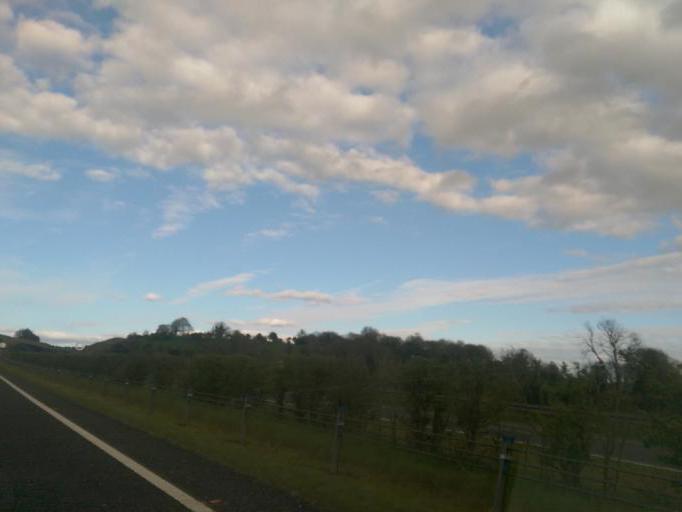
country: IE
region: Leinster
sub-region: An Mhi
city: Enfield
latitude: 53.4104
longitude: -6.7763
